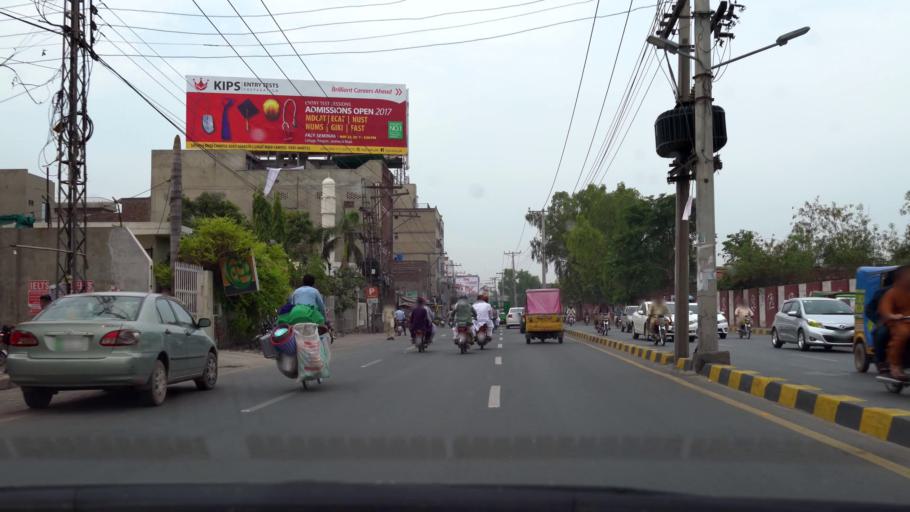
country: PK
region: Punjab
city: Faisalabad
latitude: 31.4260
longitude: 73.0724
